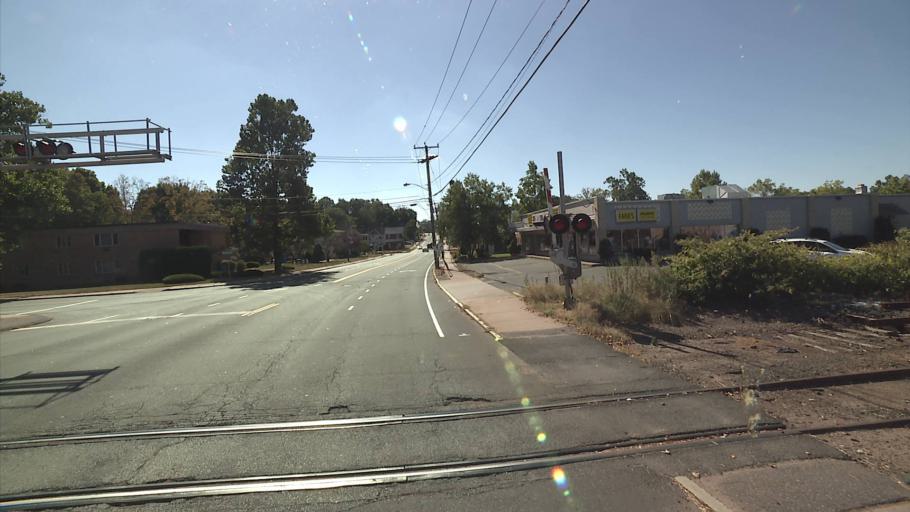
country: US
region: Connecticut
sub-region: Hartford County
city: Manchester
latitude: 41.7942
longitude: -72.5250
